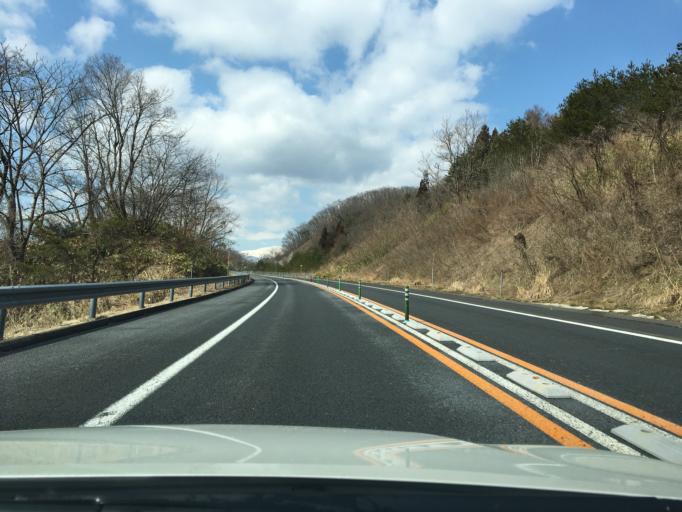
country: JP
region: Yamagata
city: Sagae
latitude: 38.3887
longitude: 140.2200
